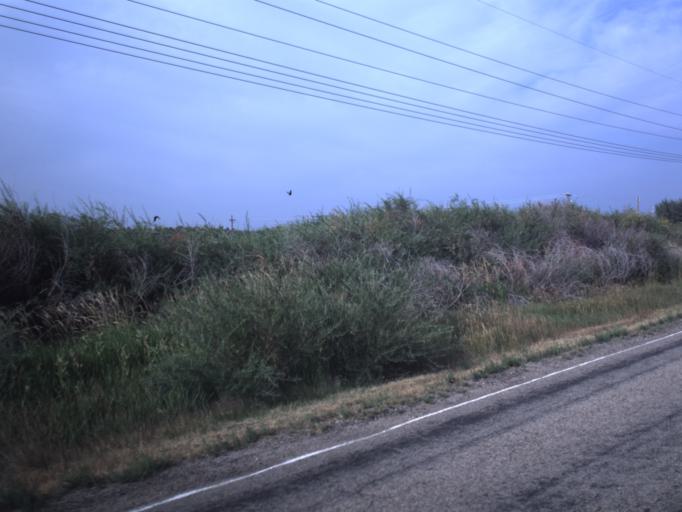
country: US
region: Utah
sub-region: Duchesne County
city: Roosevelt
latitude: 40.2580
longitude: -110.1597
